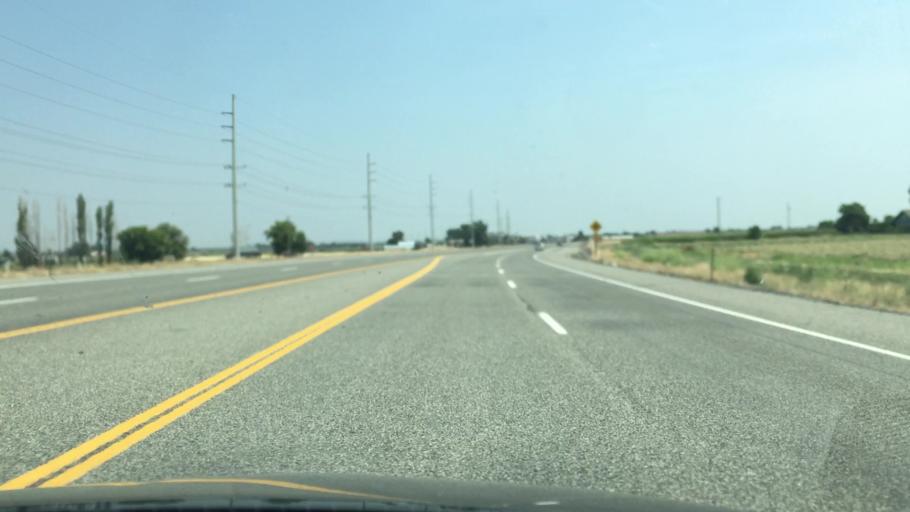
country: US
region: Idaho
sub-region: Twin Falls County
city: Twin Falls
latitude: 42.5934
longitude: -114.5191
